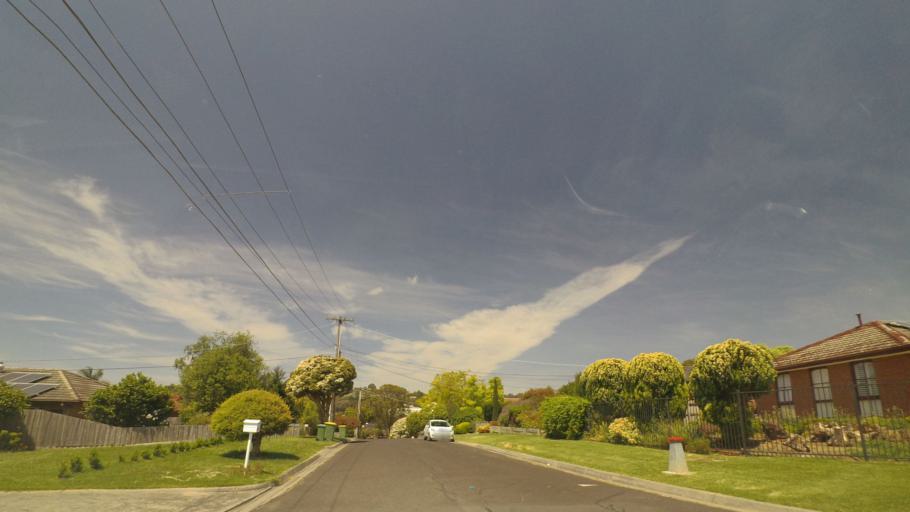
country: AU
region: Victoria
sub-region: Yarra Ranges
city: Chirnside Park
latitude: -37.7554
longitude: 145.3084
